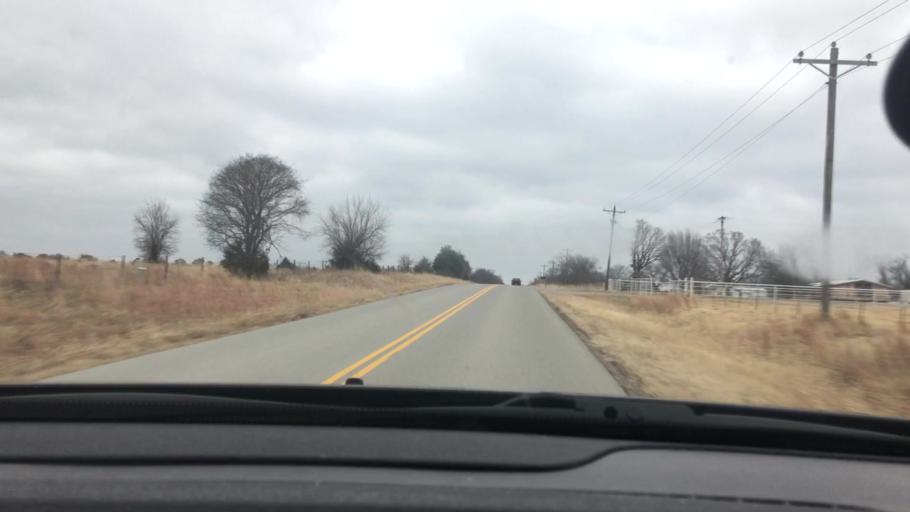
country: US
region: Oklahoma
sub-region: Atoka County
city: Atoka
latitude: 34.3351
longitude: -96.0754
